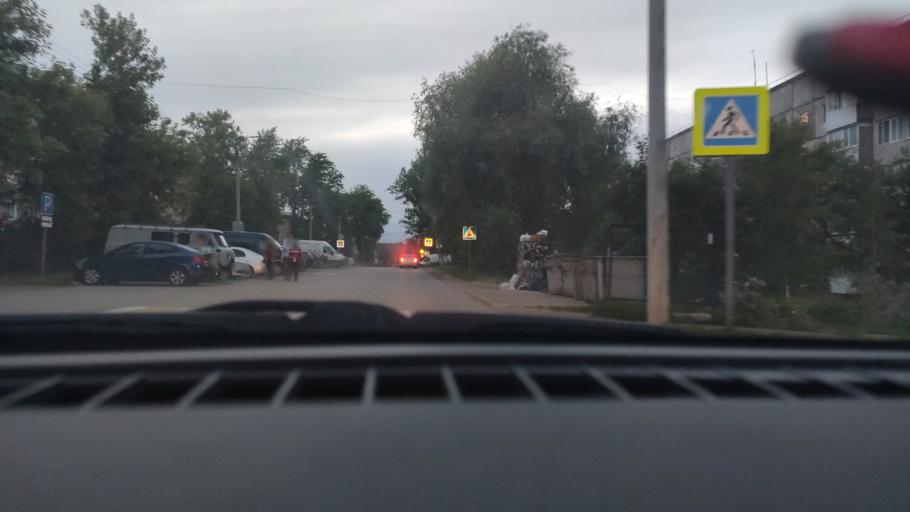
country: RU
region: Perm
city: Zvezdnyy
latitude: 57.7373
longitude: 56.3216
